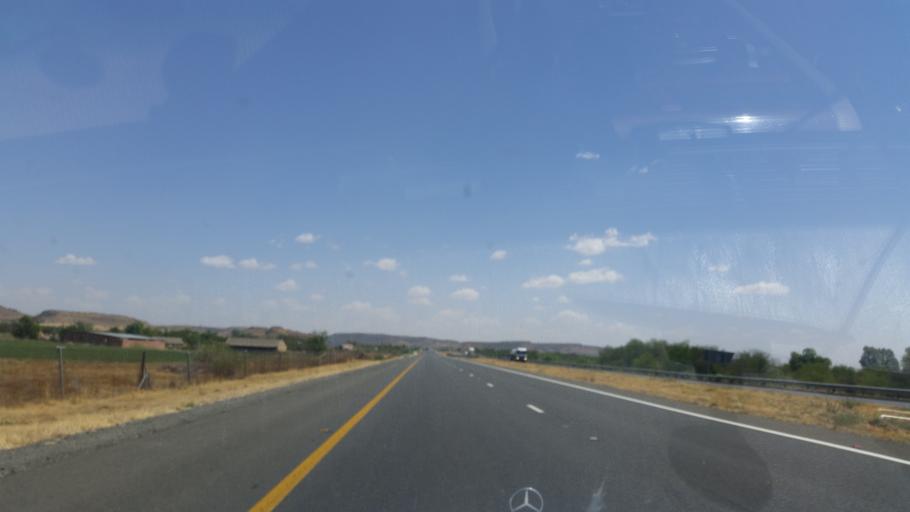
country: ZA
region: Orange Free State
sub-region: Mangaung Metropolitan Municipality
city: Bloemfontein
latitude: -28.9675
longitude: 26.3378
